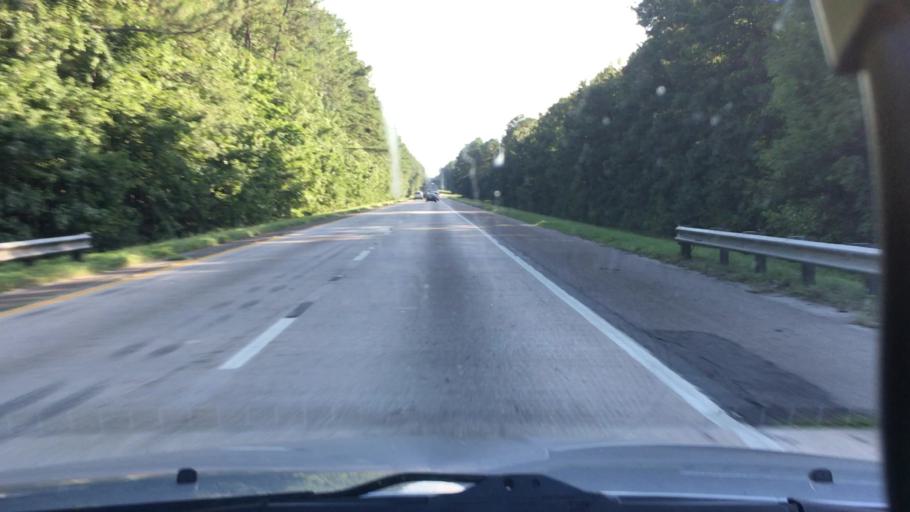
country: US
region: South Carolina
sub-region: Colleton County
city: Walterboro
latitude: 32.9057
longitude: -80.7034
